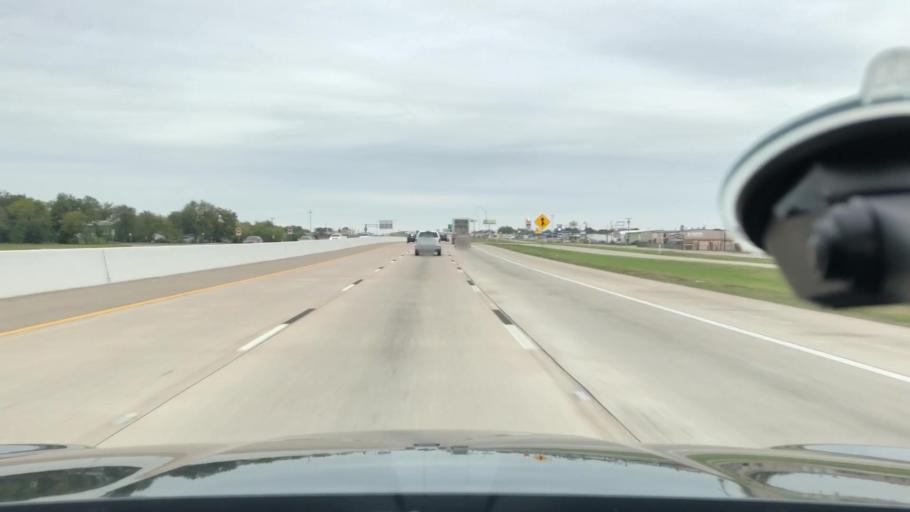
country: US
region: Texas
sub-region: McLennan County
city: Northcrest
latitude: 31.6623
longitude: -97.1002
